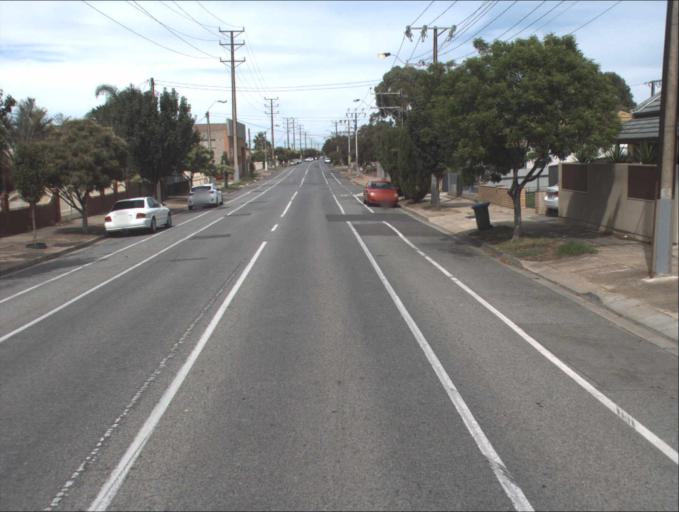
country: AU
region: South Australia
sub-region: Port Adelaide Enfield
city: Birkenhead
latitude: -34.8428
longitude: 138.4926
